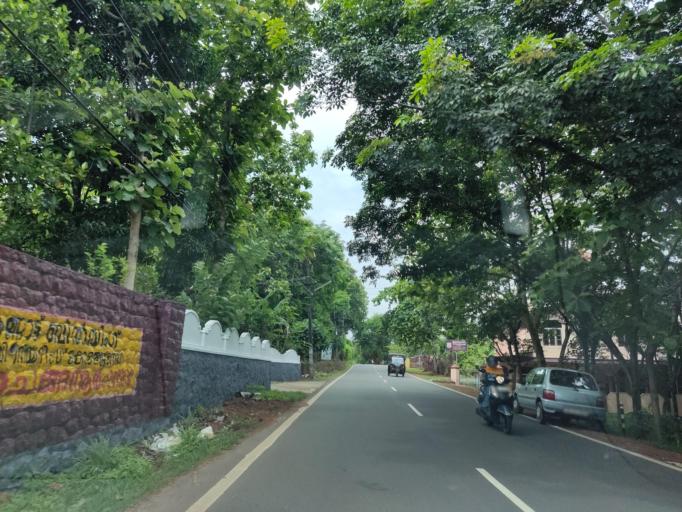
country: IN
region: Kerala
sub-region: Alappuzha
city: Chengannur
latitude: 9.2939
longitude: 76.6224
